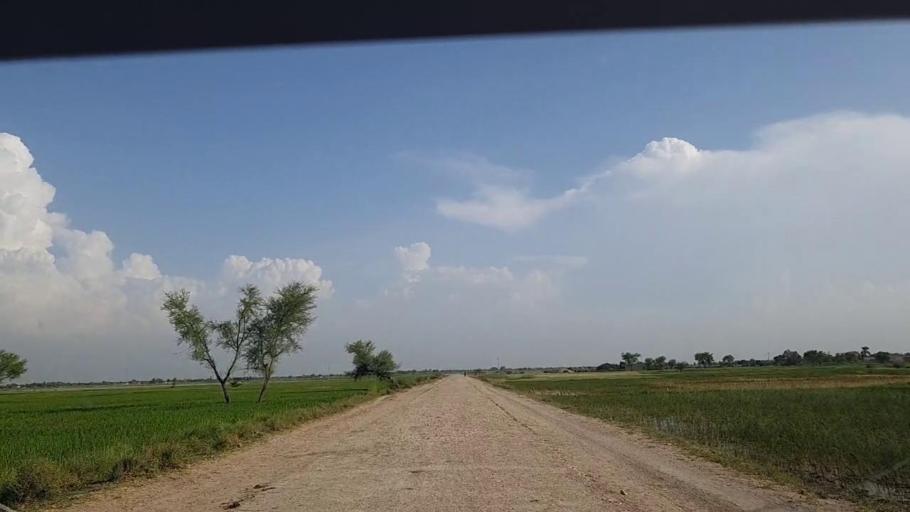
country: PK
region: Sindh
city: Khanpur
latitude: 27.8623
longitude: 69.3752
